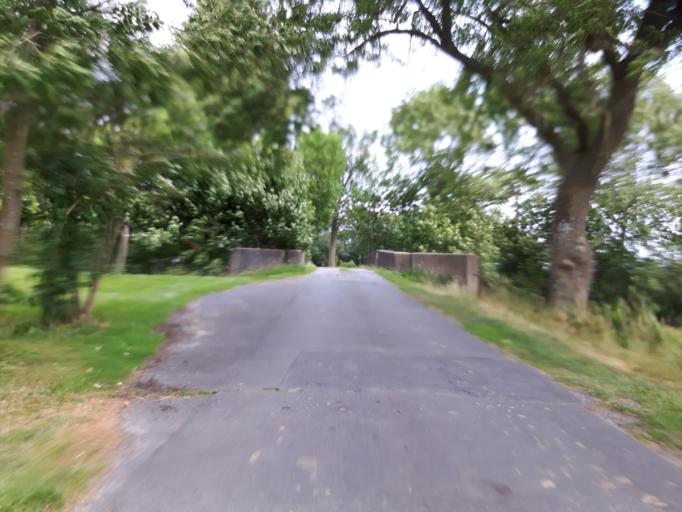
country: DE
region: Lower Saxony
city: Varel
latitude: 53.3598
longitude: 8.2045
